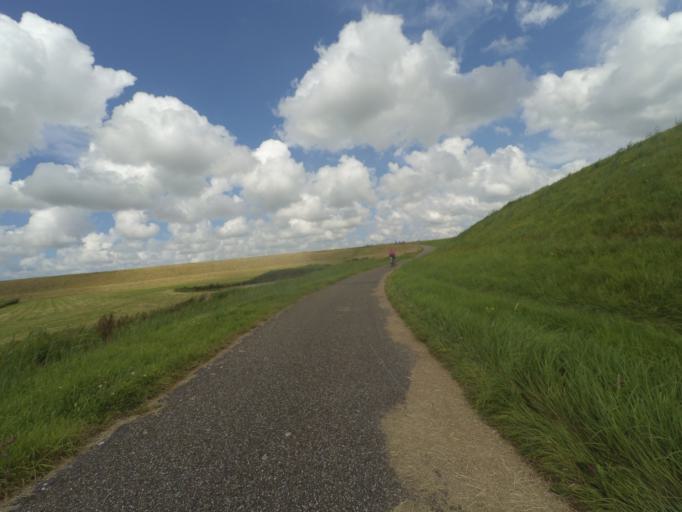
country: NL
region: North Holland
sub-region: Gemeente Texel
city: Den Burg
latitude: 53.0701
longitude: 4.8794
